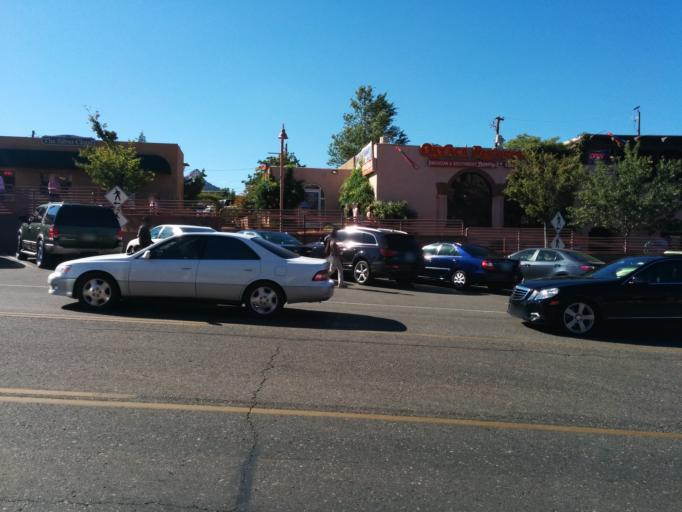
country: US
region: Arizona
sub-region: Coconino County
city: Sedona
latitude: 34.8712
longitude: -111.7596
